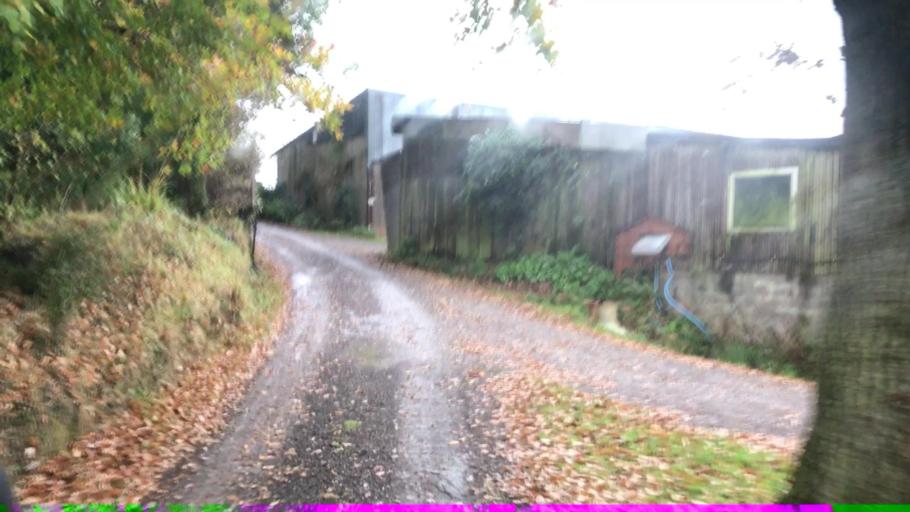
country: GB
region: England
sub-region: Devon
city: Chudleigh
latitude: 50.6416
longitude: -3.6086
